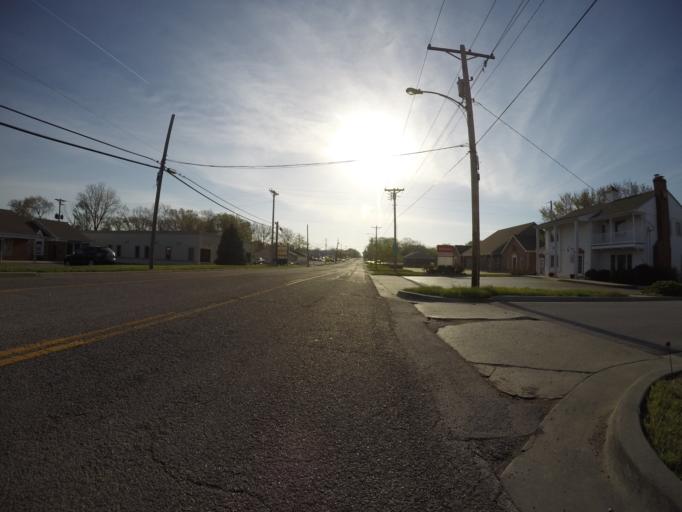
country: US
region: Missouri
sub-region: Jackson County
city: Lees Summit
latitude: 38.9111
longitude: -94.3904
